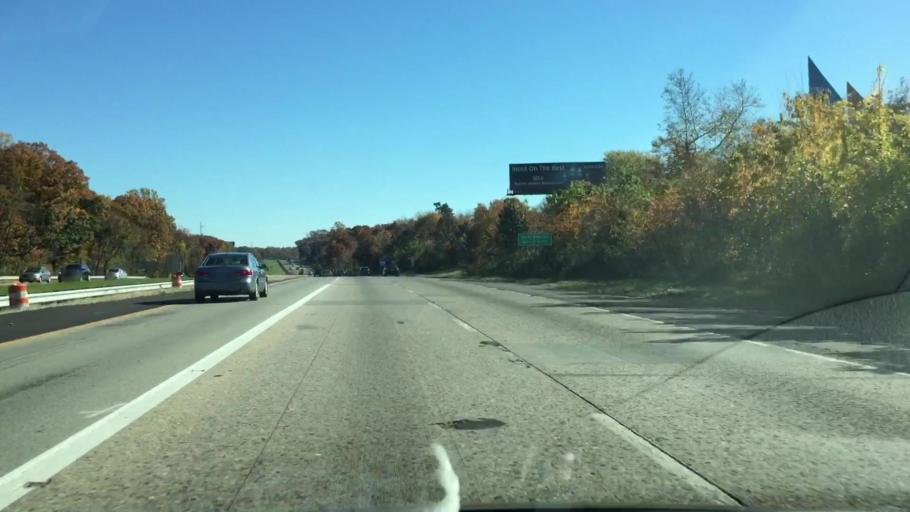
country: US
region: New Jersey
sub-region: Camden County
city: Glendora
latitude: 39.8223
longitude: -75.0789
